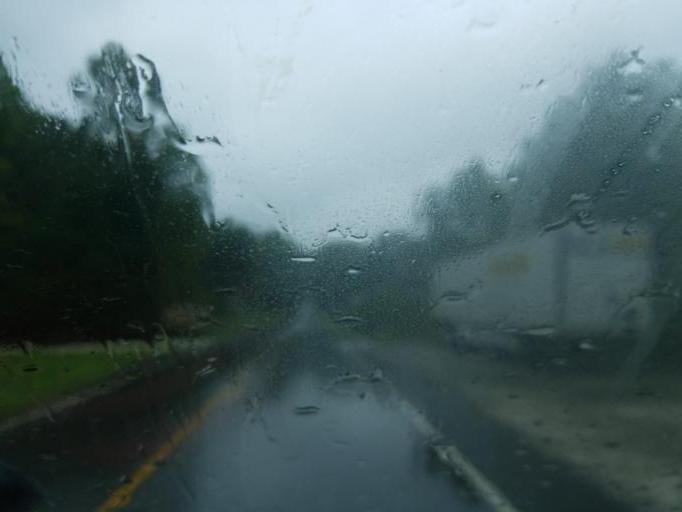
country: US
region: Kentucky
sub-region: Carter County
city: Grayson
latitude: 38.4802
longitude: -83.0322
